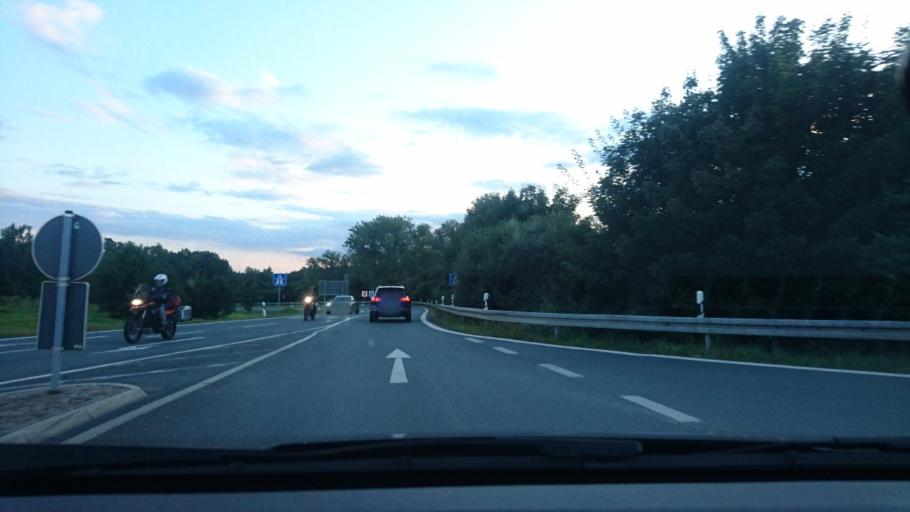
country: DE
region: Saxony
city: Treuen
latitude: 50.5540
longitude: 12.2755
